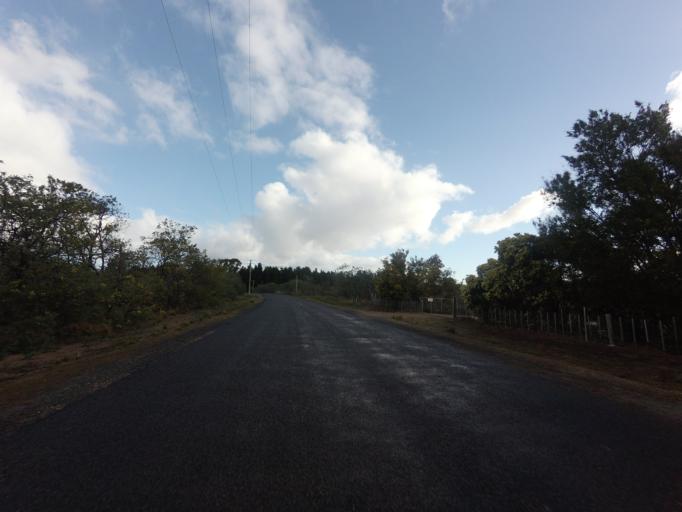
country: AU
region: Tasmania
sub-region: Break O'Day
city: St Helens
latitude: -42.1038
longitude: 148.0721
